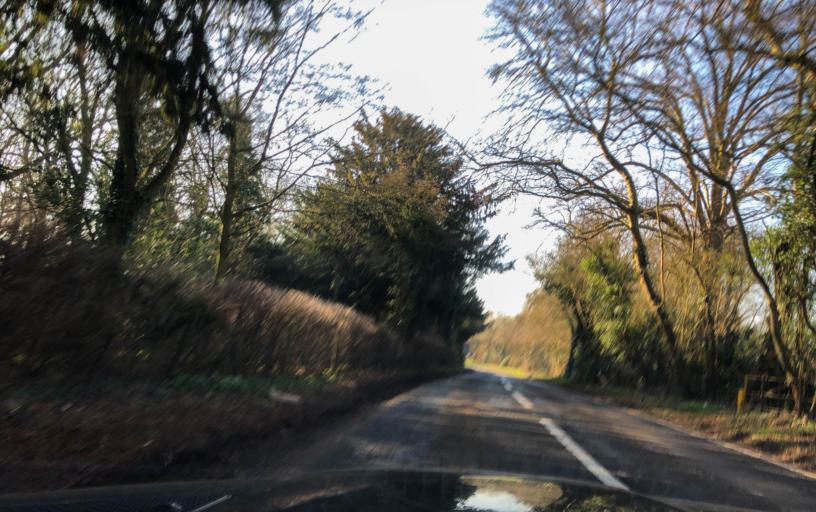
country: GB
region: England
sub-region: Warwickshire
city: Wellesbourne Mountford
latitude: 52.2147
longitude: -1.5682
